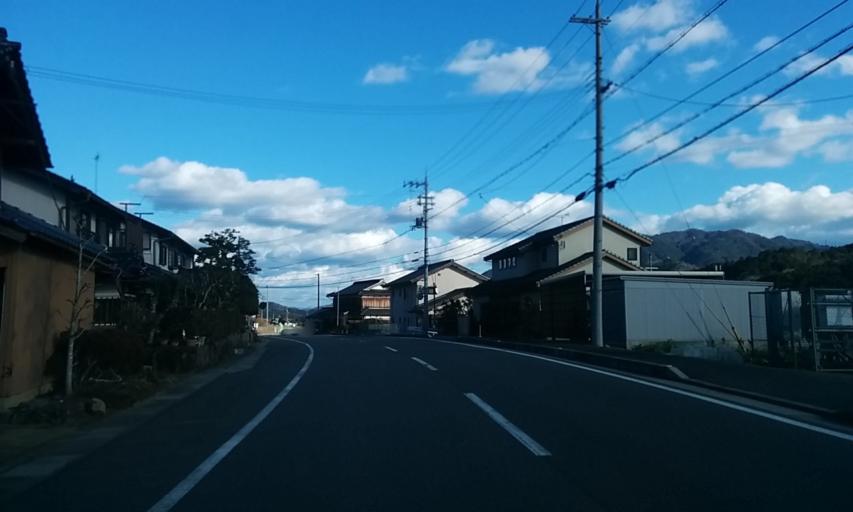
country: JP
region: Kyoto
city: Fukuchiyama
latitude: 35.2834
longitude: 135.0418
